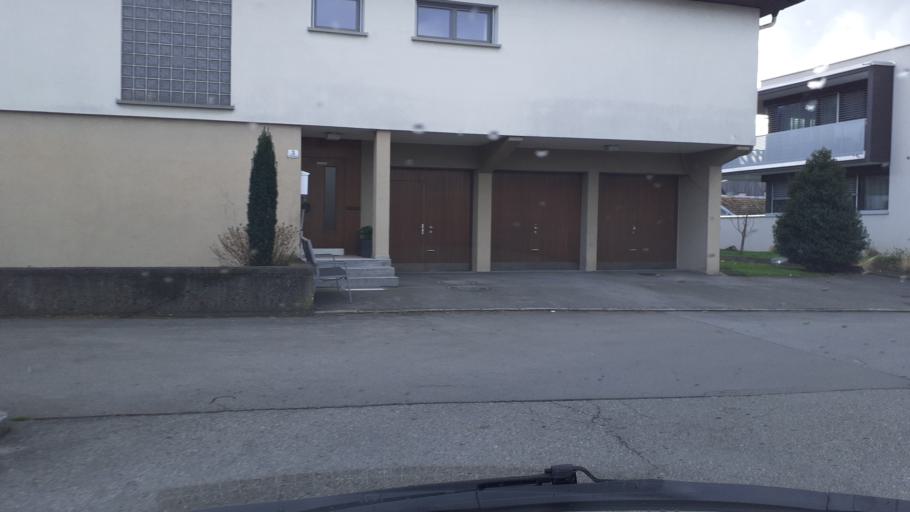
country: AT
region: Vorarlberg
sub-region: Politischer Bezirk Feldkirch
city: Gotzis
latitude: 47.3323
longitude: 9.6354
